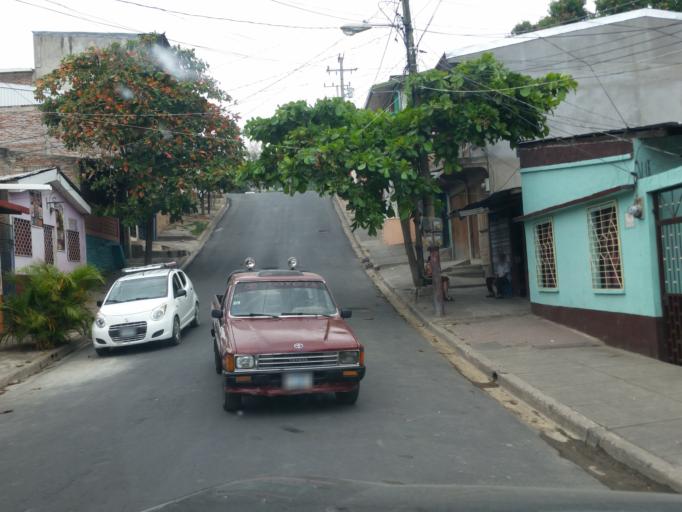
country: NI
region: Matagalpa
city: Matagalpa
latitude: 12.9294
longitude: -85.9167
